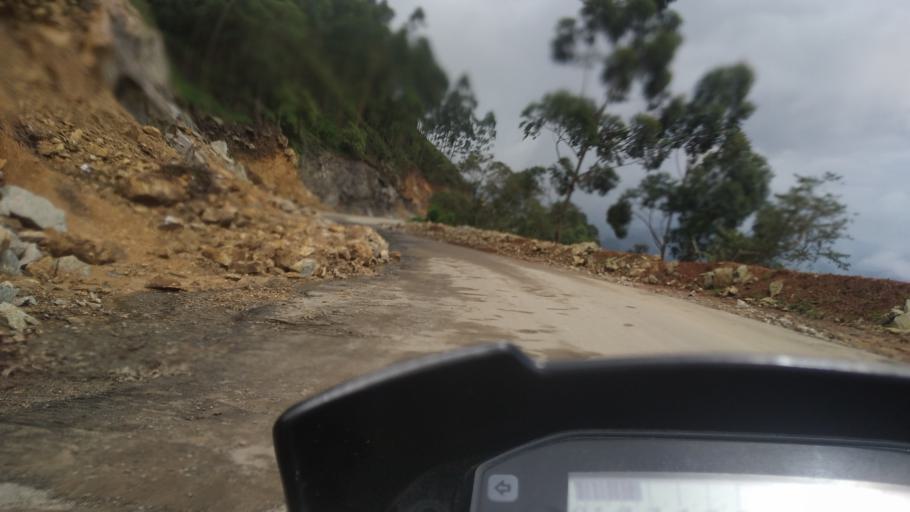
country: IN
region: Kerala
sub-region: Idukki
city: Munnar
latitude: 10.0368
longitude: 77.1336
